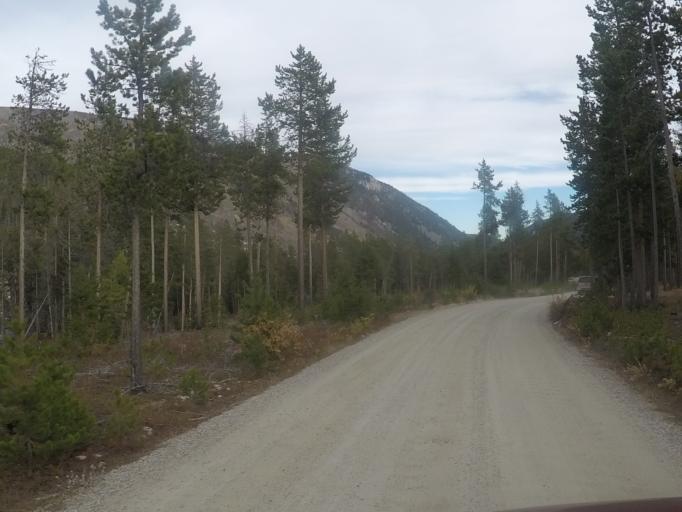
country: US
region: Montana
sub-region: Carbon County
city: Red Lodge
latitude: 45.1697
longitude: -109.4124
